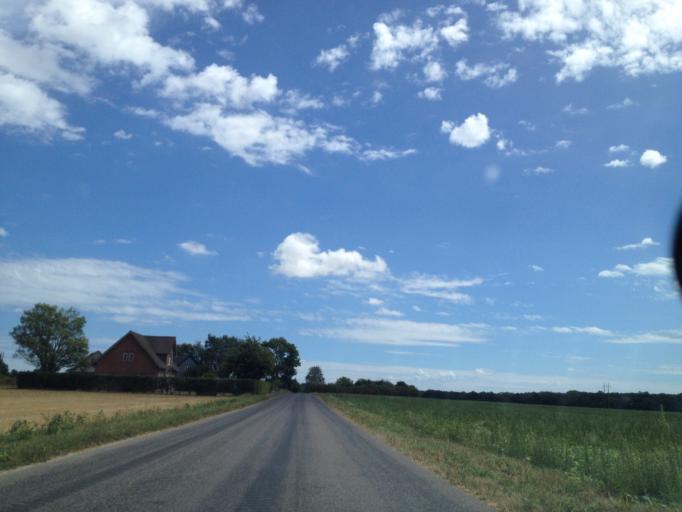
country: DK
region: Zealand
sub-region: Guldborgsund Kommune
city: Sakskobing
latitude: 54.7592
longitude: 11.6703
